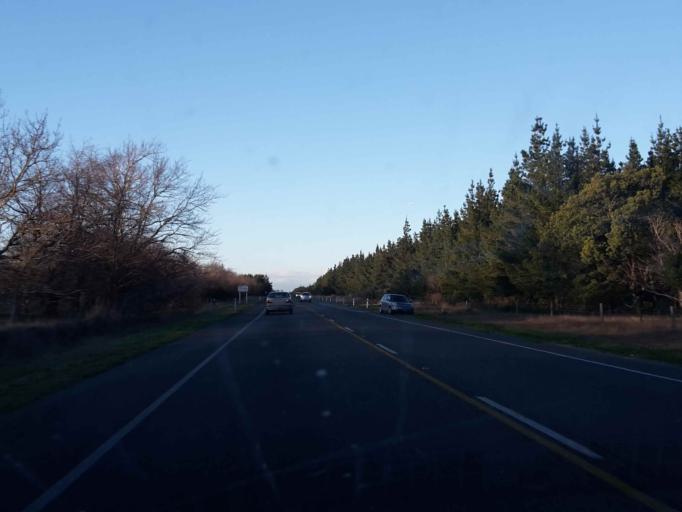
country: NZ
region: Canterbury
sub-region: Selwyn District
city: Burnham
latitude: -43.6110
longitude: 172.3260
